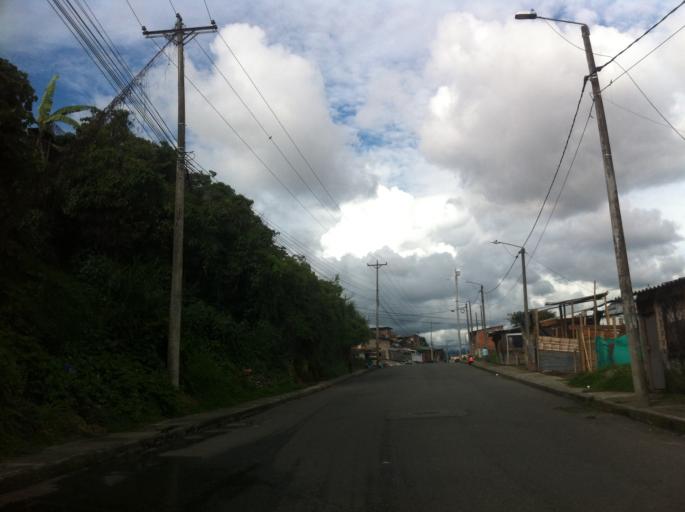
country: CO
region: Quindio
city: Armenia
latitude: 4.5271
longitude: -75.6811
